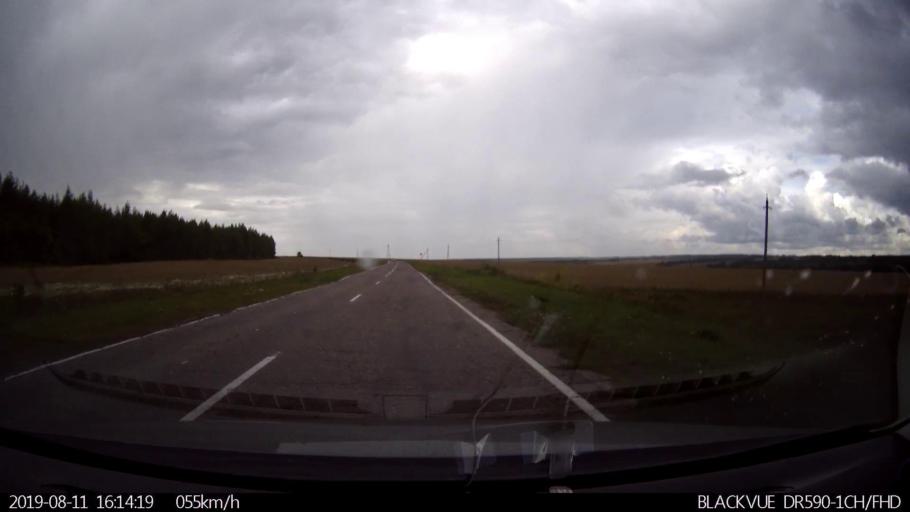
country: RU
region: Ulyanovsk
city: Ignatovka
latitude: 54.0271
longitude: 47.6343
